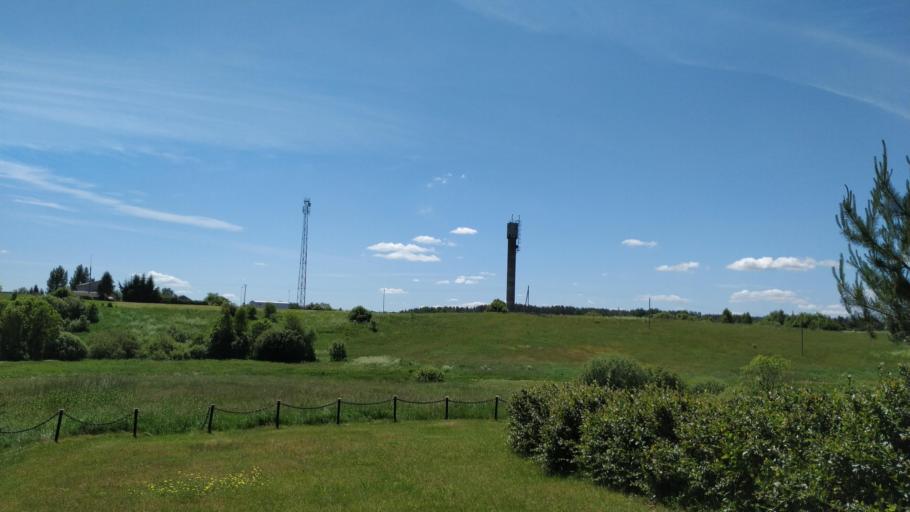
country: LT
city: Moletai
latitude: 55.0719
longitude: 25.2605
